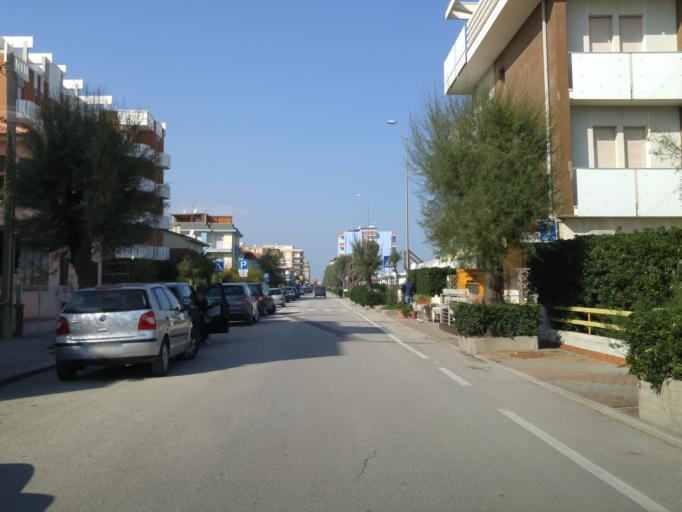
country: IT
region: The Marches
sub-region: Provincia di Pesaro e Urbino
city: Fano
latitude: 43.8446
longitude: 13.0278
